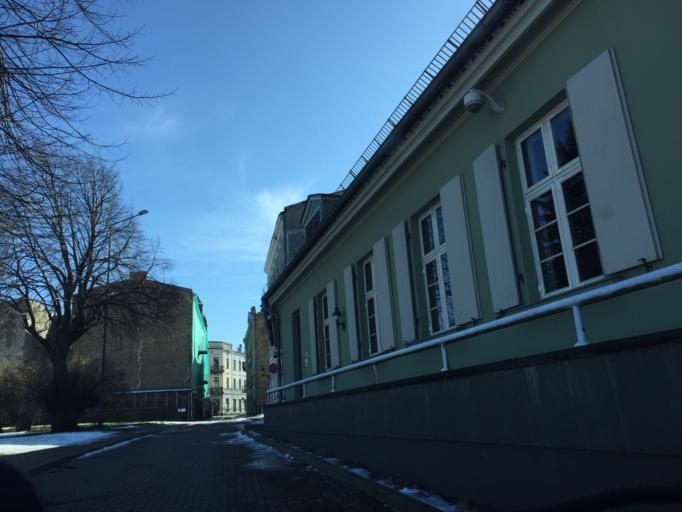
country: LV
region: Ventspils
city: Ventspils
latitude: 57.3971
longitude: 21.5618
